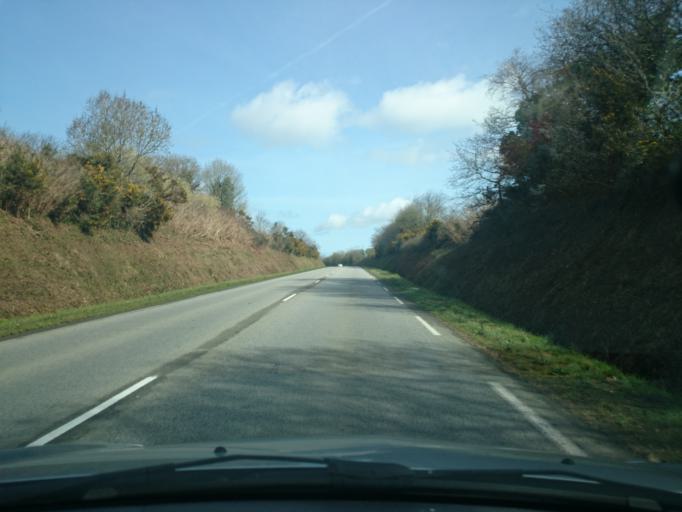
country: FR
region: Brittany
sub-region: Departement du Finistere
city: Gouesnou
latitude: 48.4507
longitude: -4.4501
